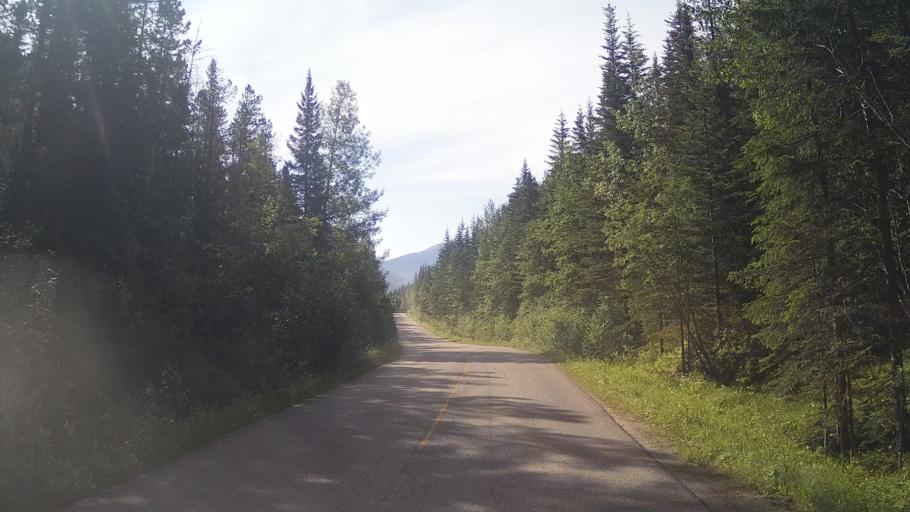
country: CA
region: Alberta
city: Hinton
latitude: 53.1768
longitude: -117.8322
